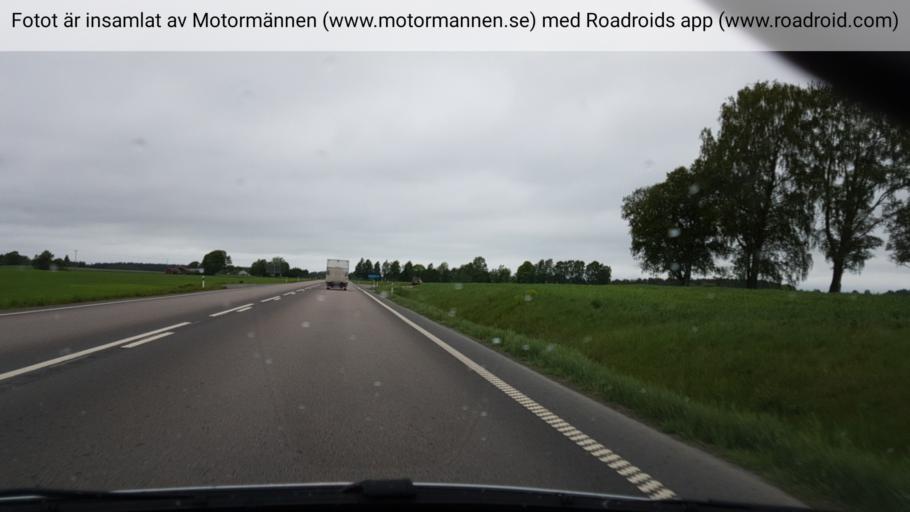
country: SE
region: Vaestra Goetaland
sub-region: Skara Kommun
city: Skara
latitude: 58.4031
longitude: 13.3933
